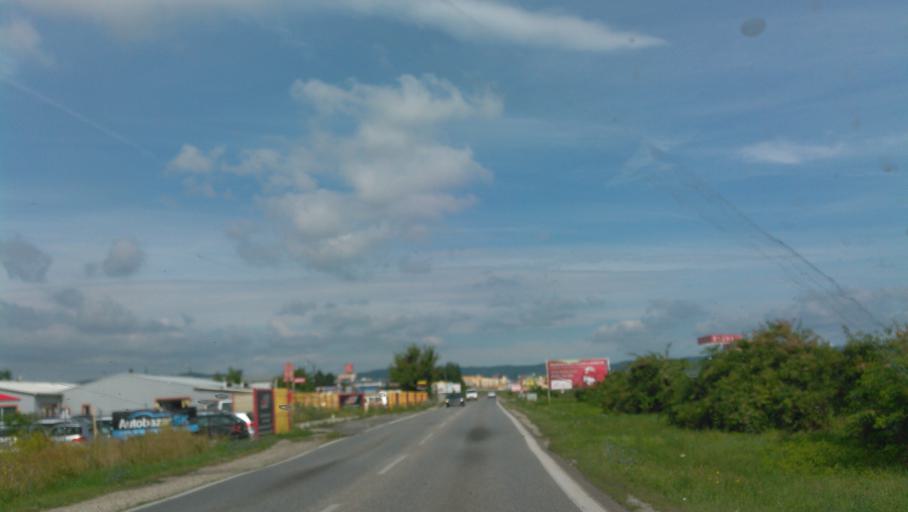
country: SK
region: Bratislavsky
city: Bratislava
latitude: 48.1573
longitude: 17.1904
